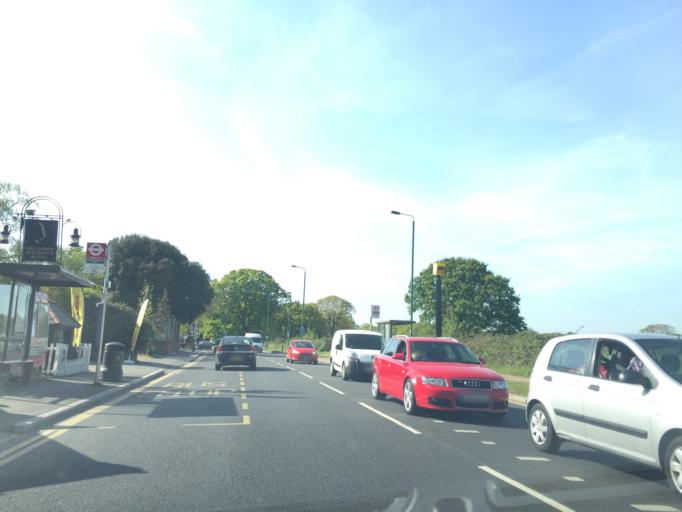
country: GB
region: England
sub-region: Greater London
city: Woodford Green
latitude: 51.5766
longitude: 0.0119
